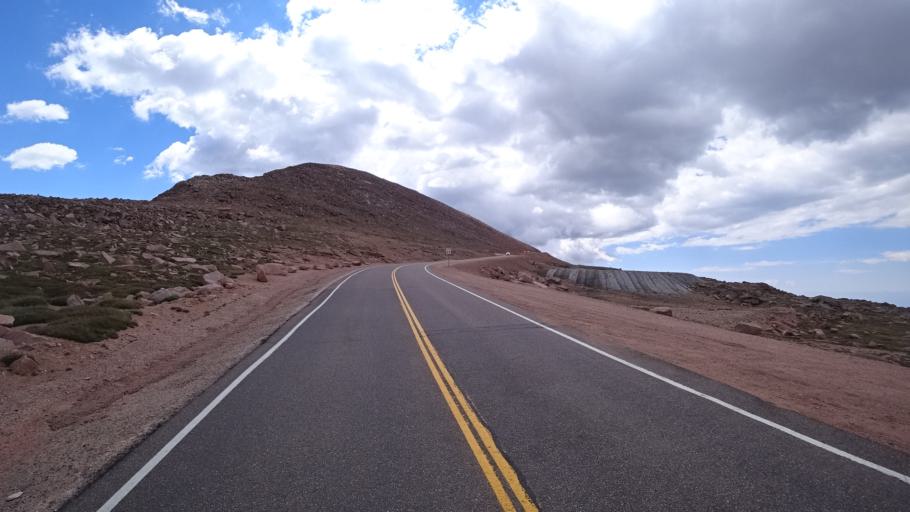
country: US
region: Colorado
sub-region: El Paso County
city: Cascade-Chipita Park
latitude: 38.8458
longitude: -105.0512
